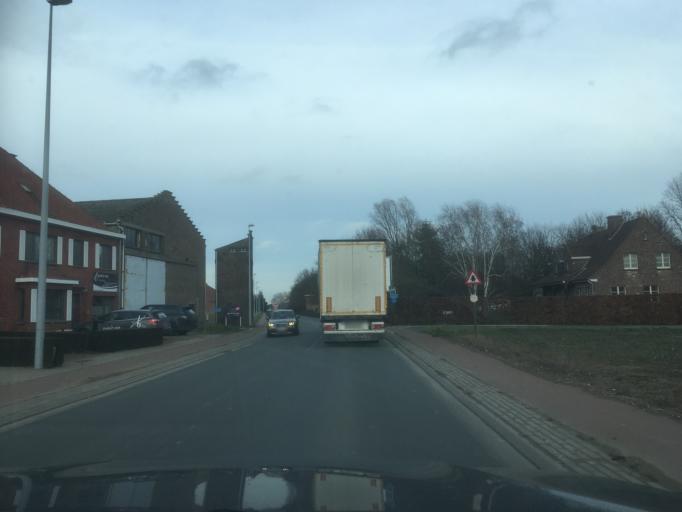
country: BE
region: Flanders
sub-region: Provincie West-Vlaanderen
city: Oostrozebeke
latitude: 50.9117
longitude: 3.3527
